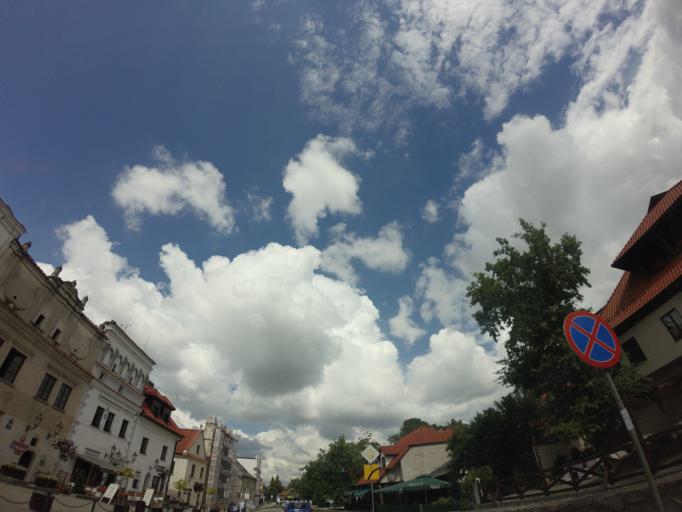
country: PL
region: Lublin Voivodeship
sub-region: Powiat pulawski
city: Kazimierz Dolny
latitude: 51.3219
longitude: 21.9462
